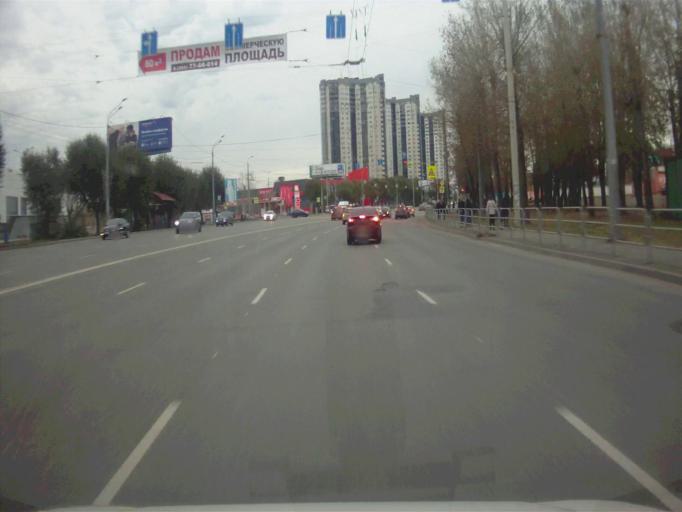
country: RU
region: Chelyabinsk
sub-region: Gorod Chelyabinsk
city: Chelyabinsk
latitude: 55.1708
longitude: 61.3691
